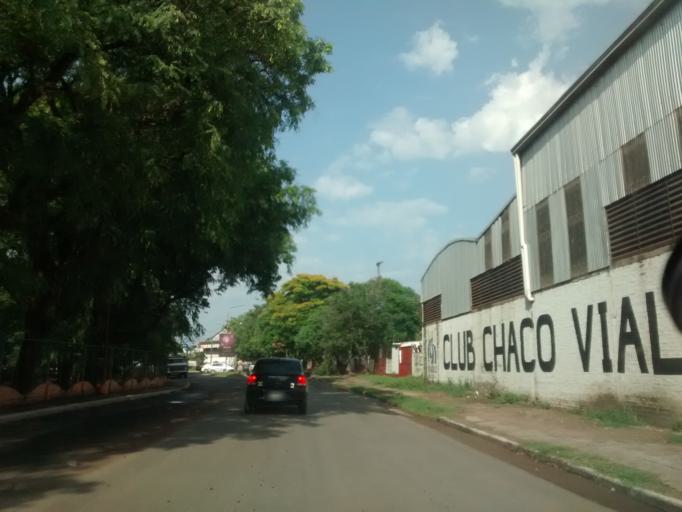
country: AR
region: Chaco
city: Resistencia
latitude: -27.4363
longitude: -58.9830
